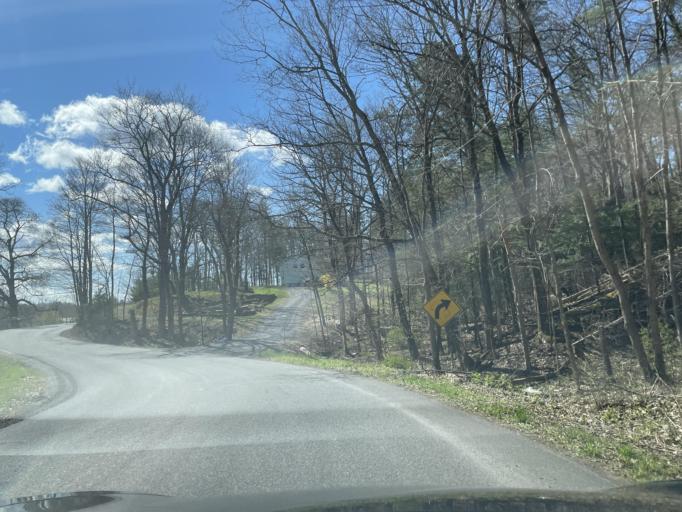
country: US
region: New York
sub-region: Ulster County
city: Saugerties South
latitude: 42.0638
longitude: -73.9884
